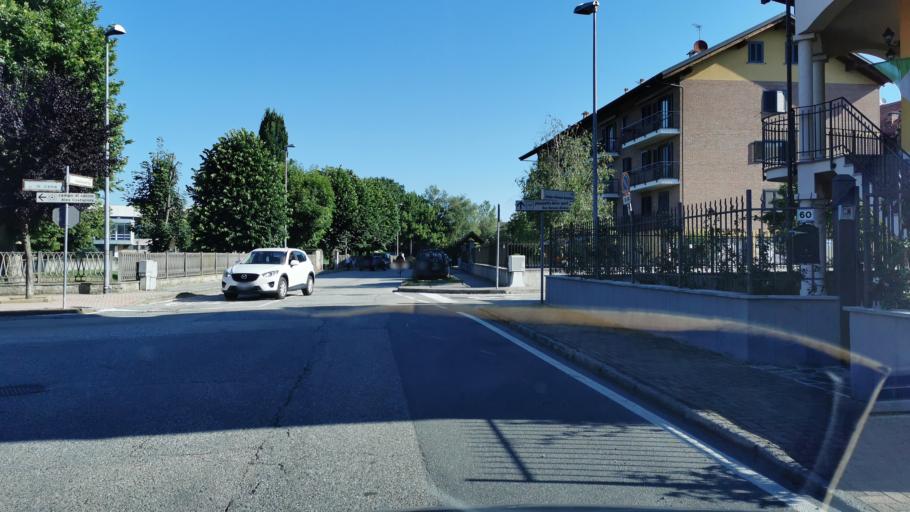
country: IT
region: Piedmont
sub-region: Provincia di Torino
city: Brandizzo
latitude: 45.1832
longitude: 7.8403
